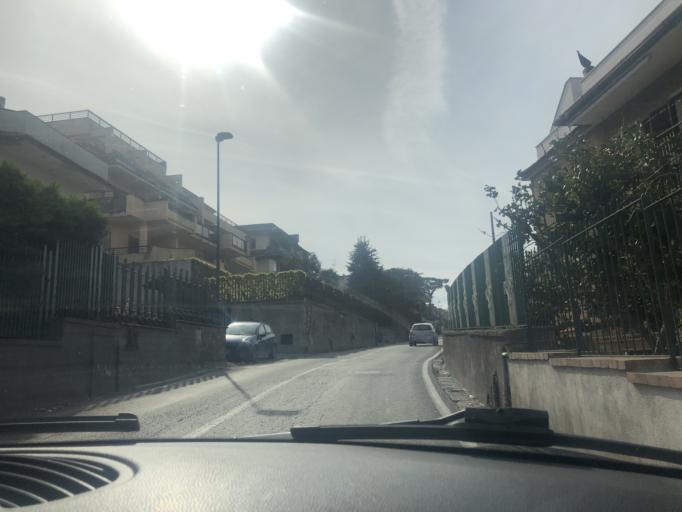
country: IT
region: Campania
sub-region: Provincia di Napoli
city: Torre Caracciolo
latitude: 40.8679
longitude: 14.1966
